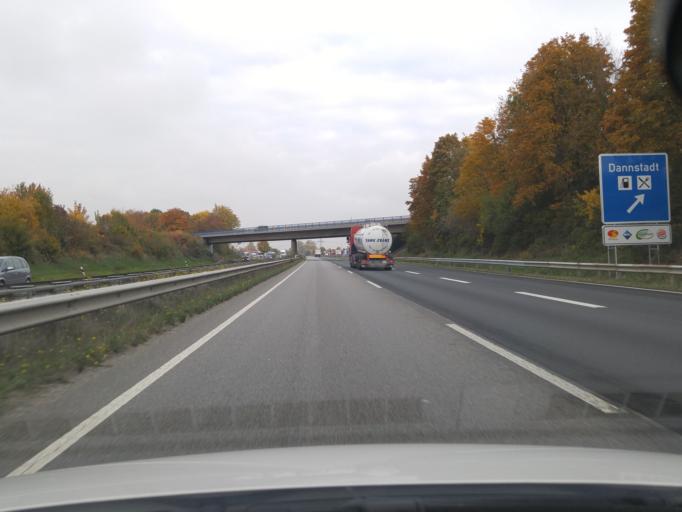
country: DE
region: Rheinland-Pfalz
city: Mutterstadt
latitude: 49.4060
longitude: 8.3409
